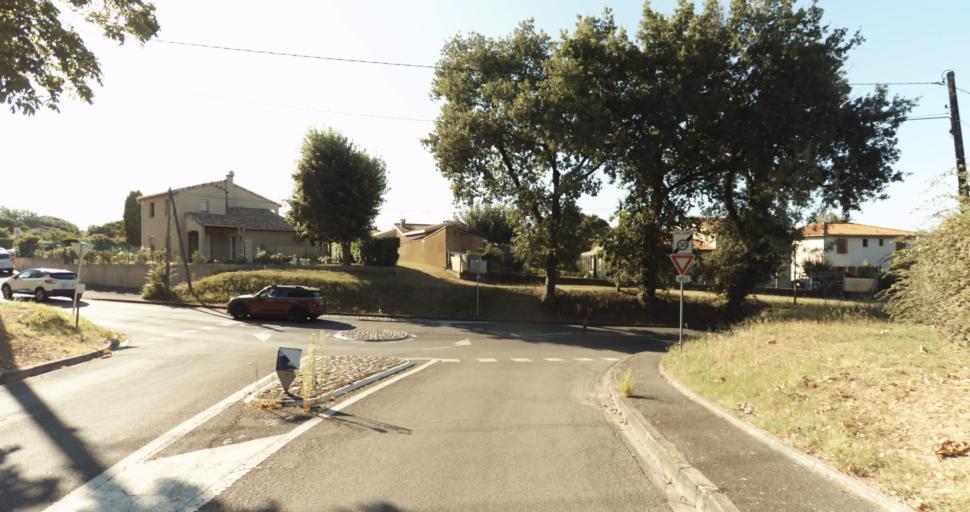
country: FR
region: Midi-Pyrenees
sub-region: Departement de la Haute-Garonne
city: L'Union
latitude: 43.6634
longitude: 1.4872
